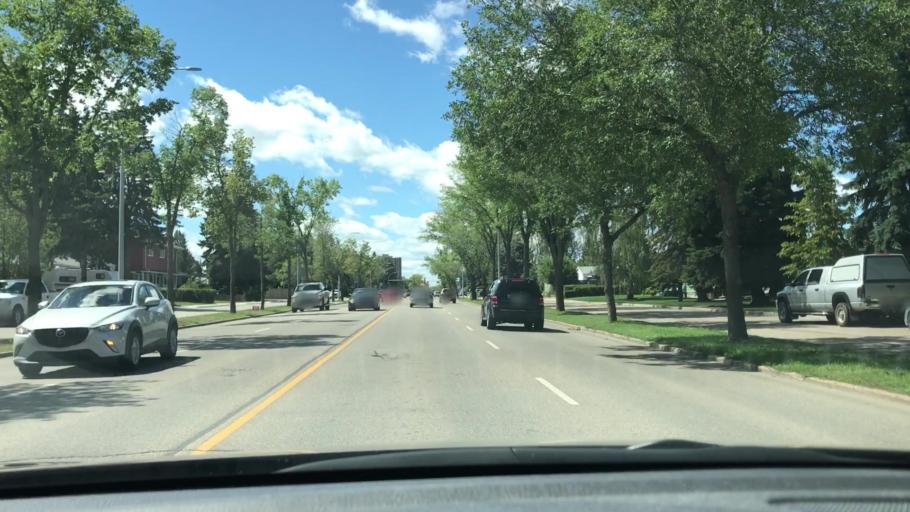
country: CA
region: Alberta
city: Edmonton
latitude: 53.5194
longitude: -113.5729
